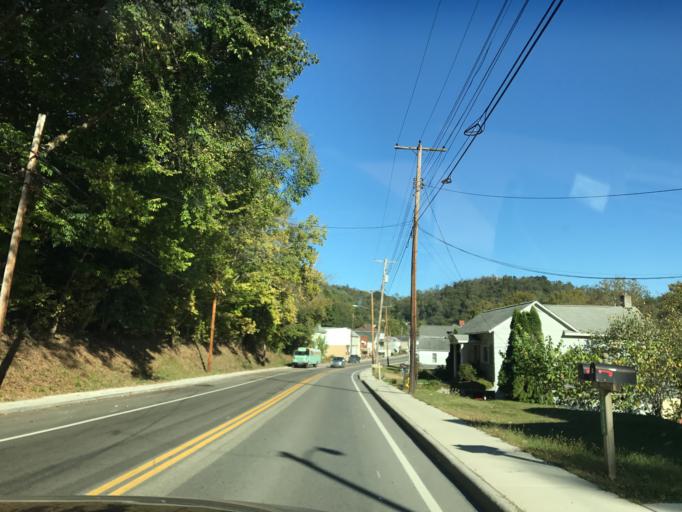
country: US
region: Ohio
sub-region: Belmont County
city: Wolfhurst
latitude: 40.0746
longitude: -80.7964
